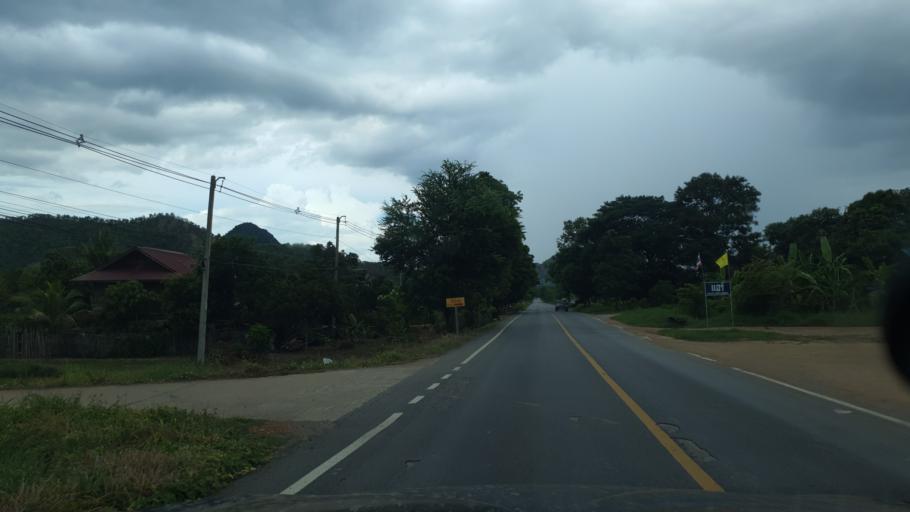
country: TH
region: Sukhothai
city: Thung Saliam
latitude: 17.3358
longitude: 99.4789
